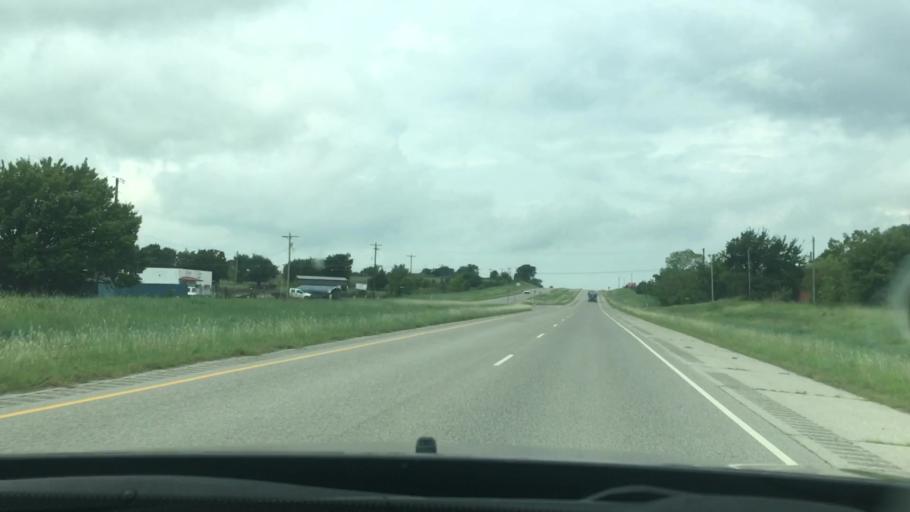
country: US
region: Oklahoma
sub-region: Carter County
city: Wilson
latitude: 34.1731
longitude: -97.4552
